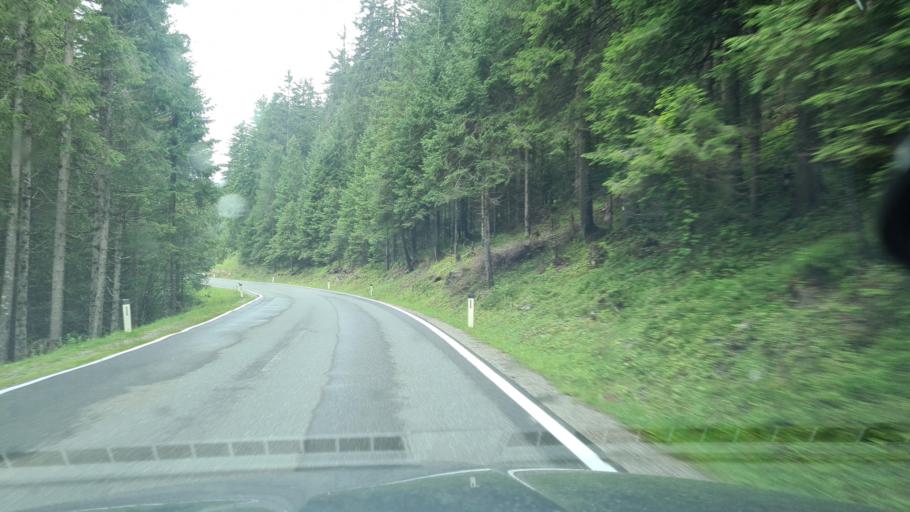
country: AT
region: Salzburg
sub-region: Politischer Bezirk Sankt Johann im Pongau
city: Radstadt
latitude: 47.3303
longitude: 13.4451
